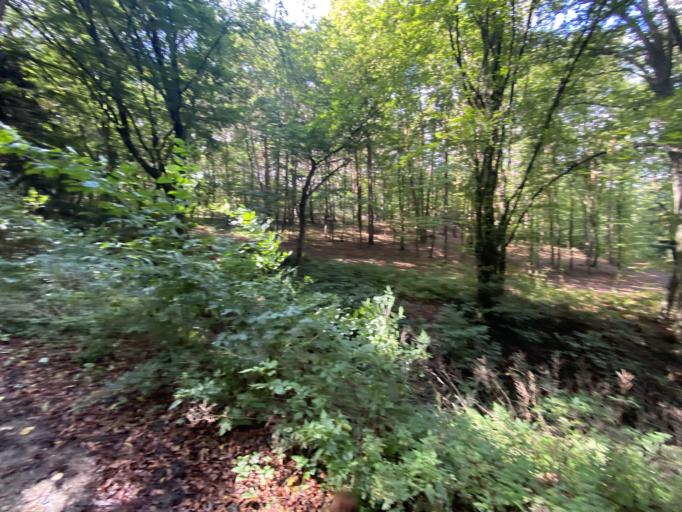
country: AT
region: Burgenland
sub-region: Politischer Bezirk Oberpullendorf
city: Kobersdorf
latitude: 47.5850
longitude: 16.3832
